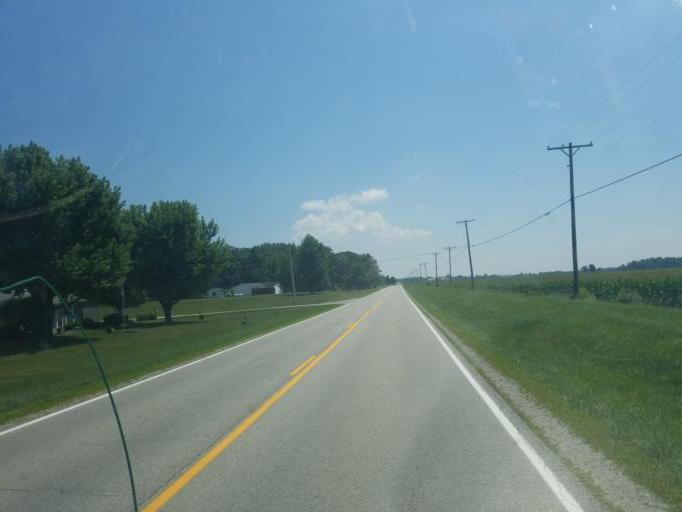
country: US
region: Ohio
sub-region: Shelby County
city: Anna
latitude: 40.4176
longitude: -84.1759
